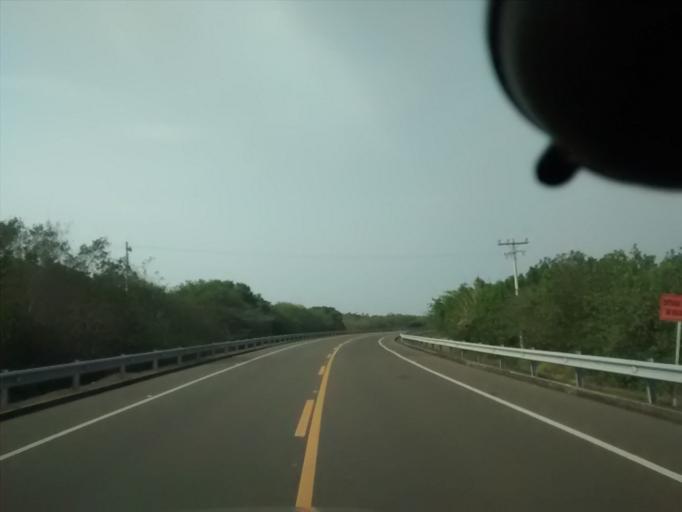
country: CO
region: Bolivar
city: Clemencia
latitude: 10.6521
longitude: -75.3969
